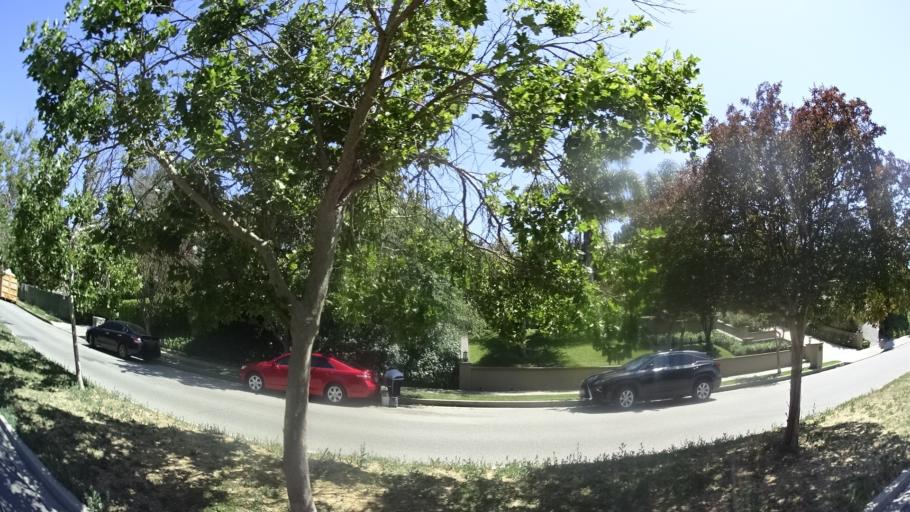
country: US
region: California
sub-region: Los Angeles County
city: Sherman Oaks
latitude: 34.1462
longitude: -118.4914
